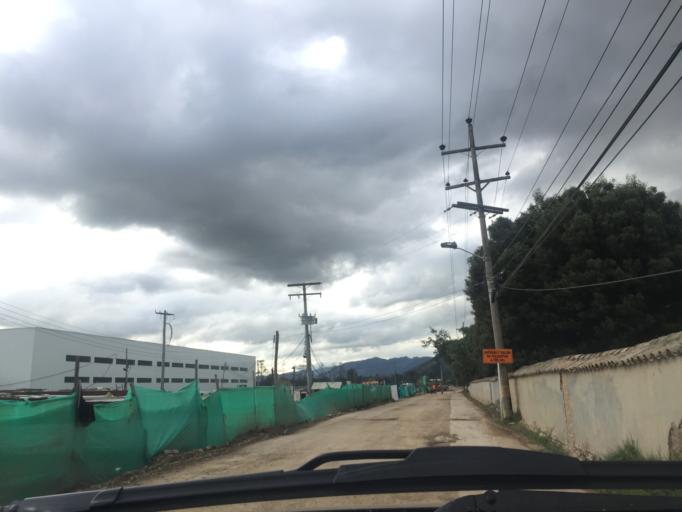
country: CO
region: Cundinamarca
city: Sopo
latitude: 4.9345
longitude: -73.9372
